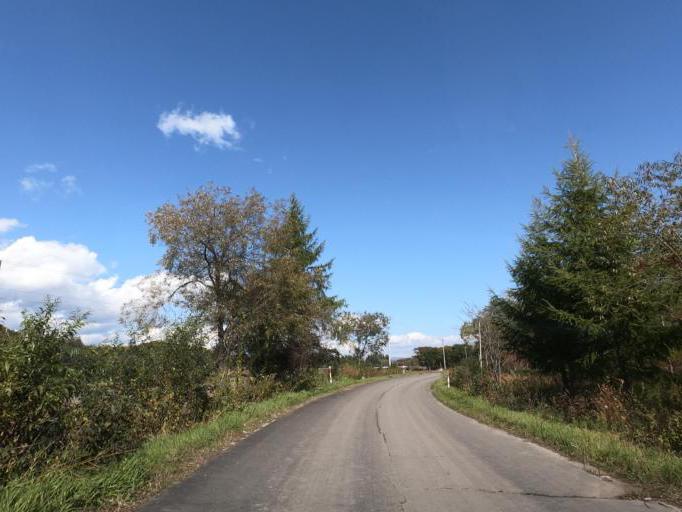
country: JP
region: Hokkaido
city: Otofuke
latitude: 43.2343
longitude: 143.2651
